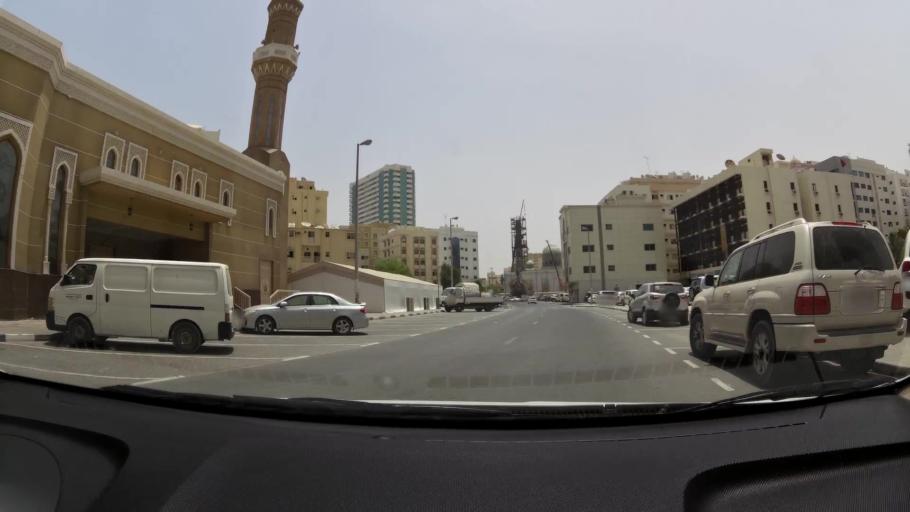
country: AE
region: Ash Shariqah
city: Sharjah
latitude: 25.3526
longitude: 55.3877
